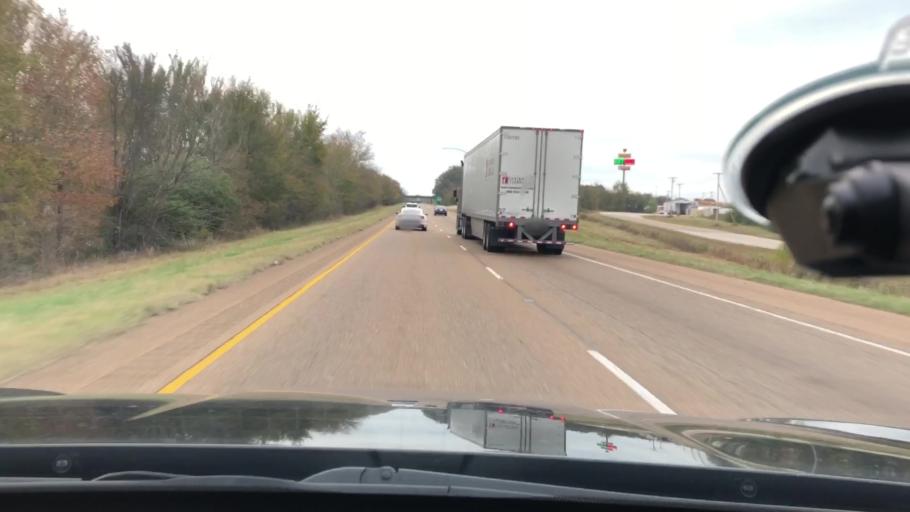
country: US
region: Arkansas
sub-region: Nevada County
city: Prescott
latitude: 33.8271
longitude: -93.4007
